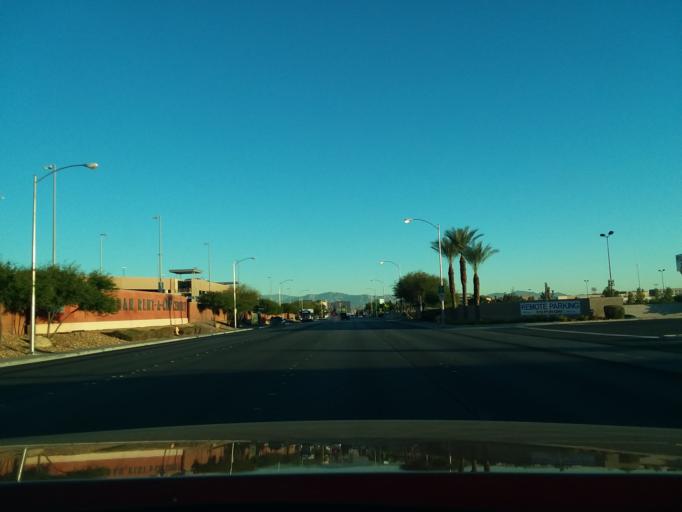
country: US
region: Nevada
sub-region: Clark County
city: Paradise
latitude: 36.0596
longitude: -115.1634
